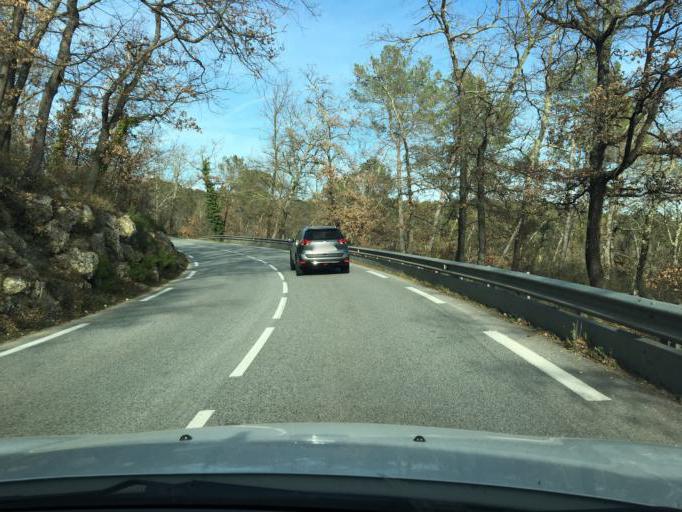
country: FR
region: Provence-Alpes-Cote d'Azur
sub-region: Departement du Var
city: Saint-Paul-en-Foret
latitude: 43.5836
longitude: 6.6686
